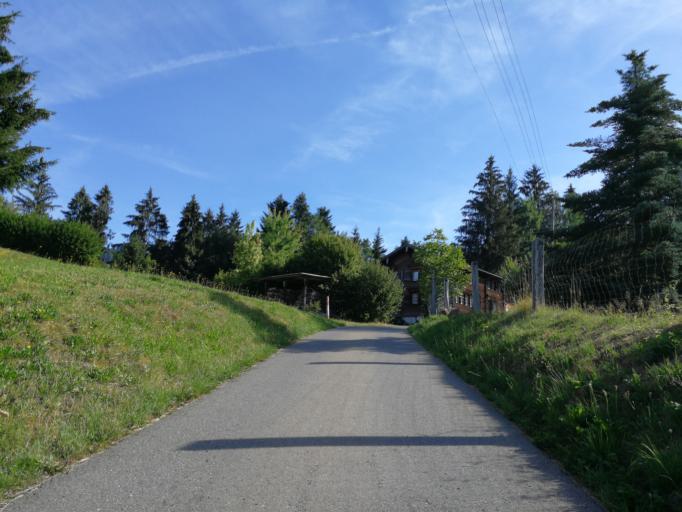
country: CH
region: Saint Gallen
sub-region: Wahlkreis See-Gaster
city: Gommiswald
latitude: 47.2455
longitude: 9.0163
